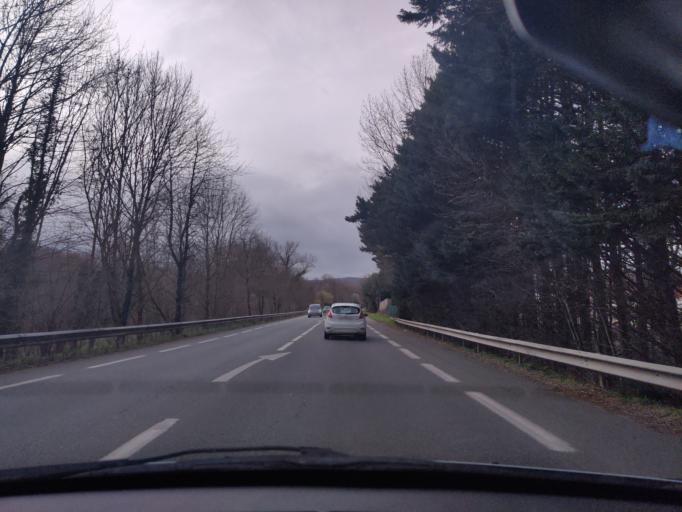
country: FR
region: Auvergne
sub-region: Departement du Puy-de-Dome
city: Marsat
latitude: 45.8825
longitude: 3.0861
